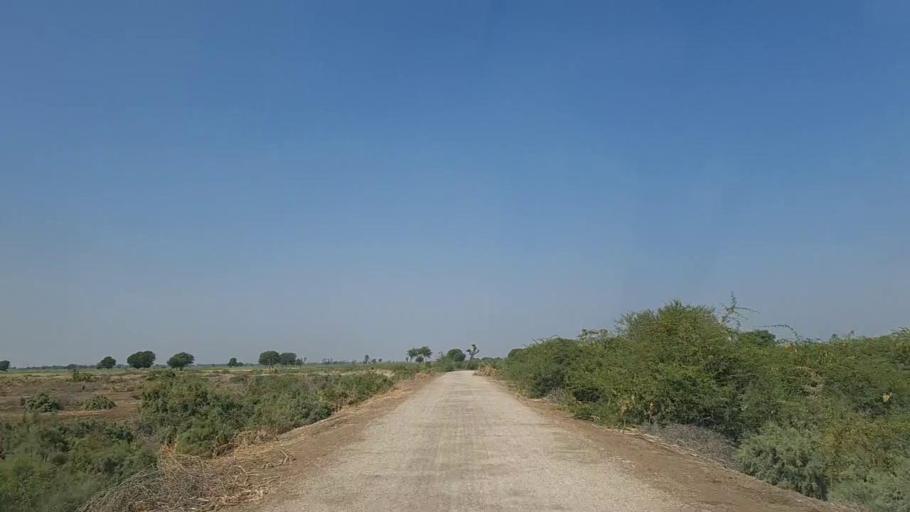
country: PK
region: Sindh
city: Digri
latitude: 25.1961
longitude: 69.1393
